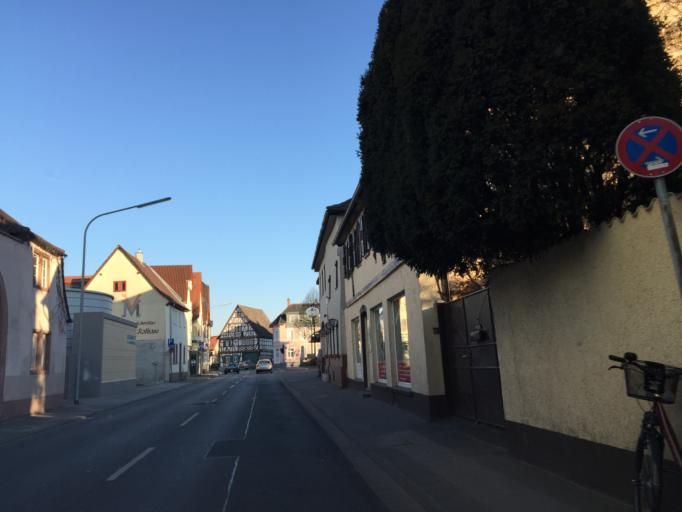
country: DE
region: Hesse
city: Pfungstadt
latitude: 49.8025
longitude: 8.5967
